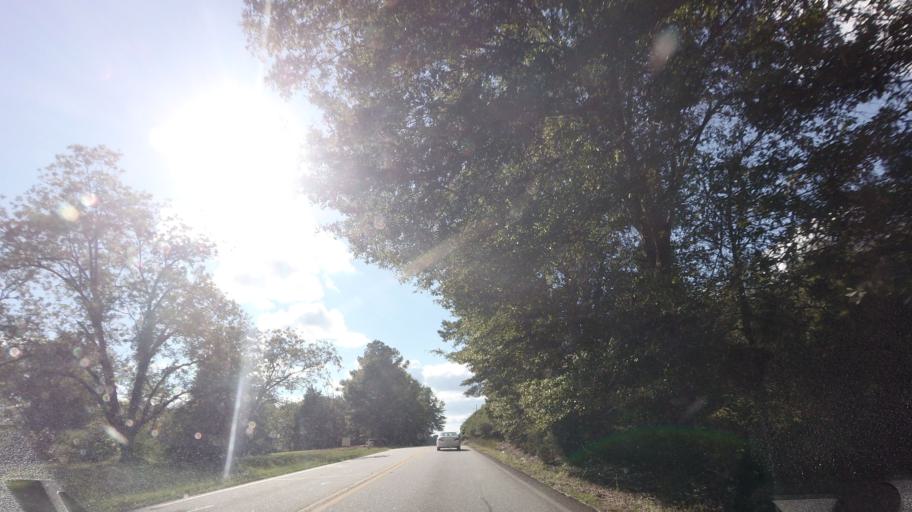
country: US
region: Georgia
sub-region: Lamar County
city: Barnesville
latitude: 33.0516
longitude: -84.1196
